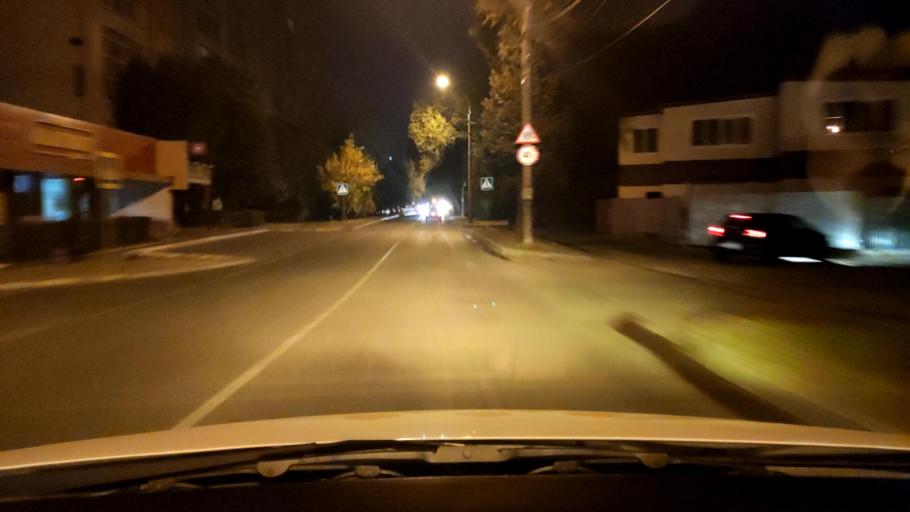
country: RU
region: Voronezj
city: Voronezh
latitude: 51.6456
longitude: 39.1742
